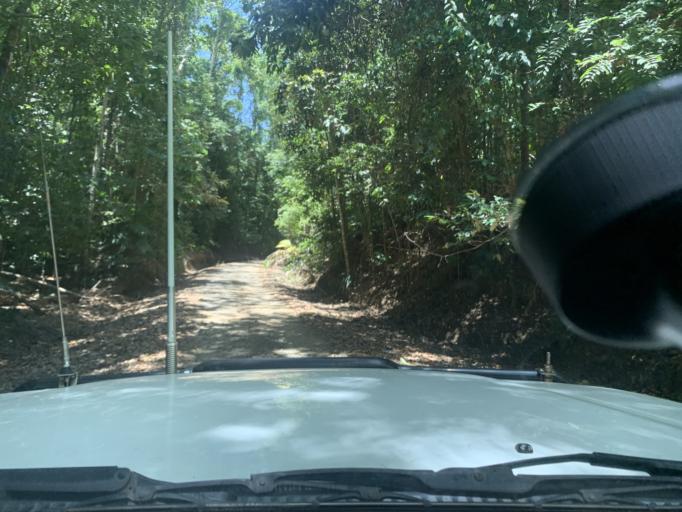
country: AU
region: Queensland
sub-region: Cairns
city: Redlynch
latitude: -16.9678
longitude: 145.6489
